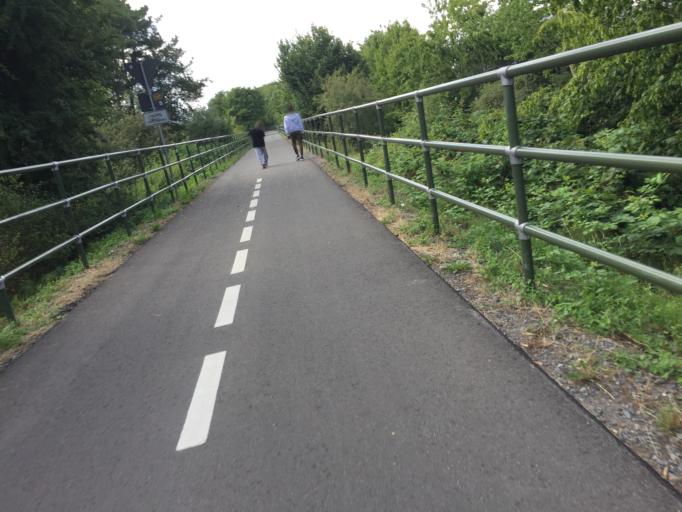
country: DE
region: Hesse
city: Schwalmstadt
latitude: 50.9116
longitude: 9.1986
